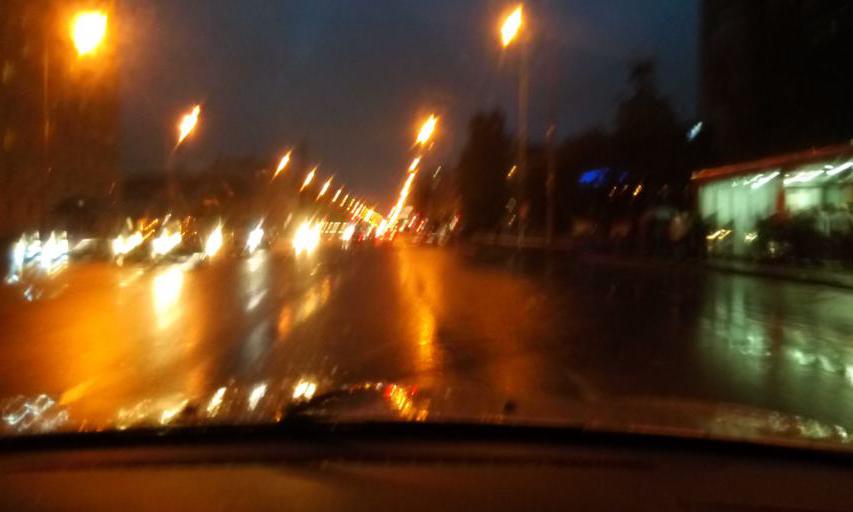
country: KZ
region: Astana Qalasy
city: Astana
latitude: 51.1747
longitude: 71.4066
